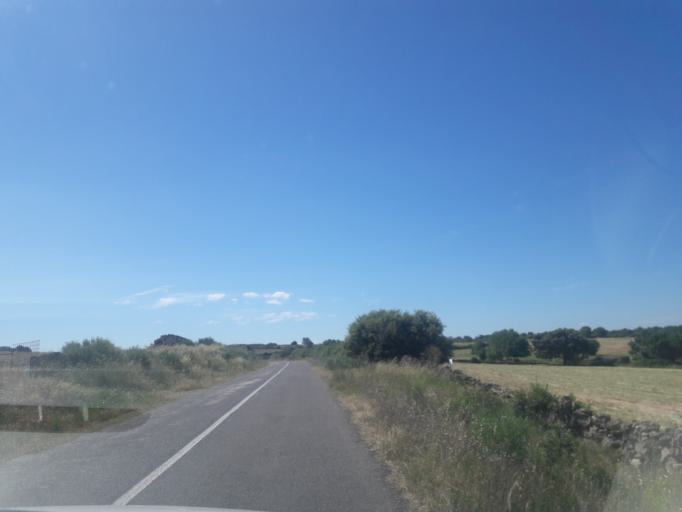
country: ES
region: Castille and Leon
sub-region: Provincia de Salamanca
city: Lumbrales
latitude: 40.9802
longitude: -6.7305
